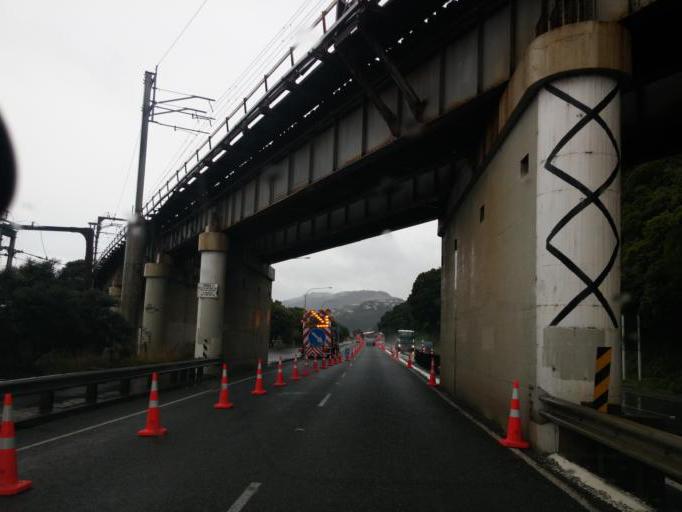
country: NZ
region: Wellington
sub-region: Wellington City
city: Wellington
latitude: -41.2527
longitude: 174.8045
